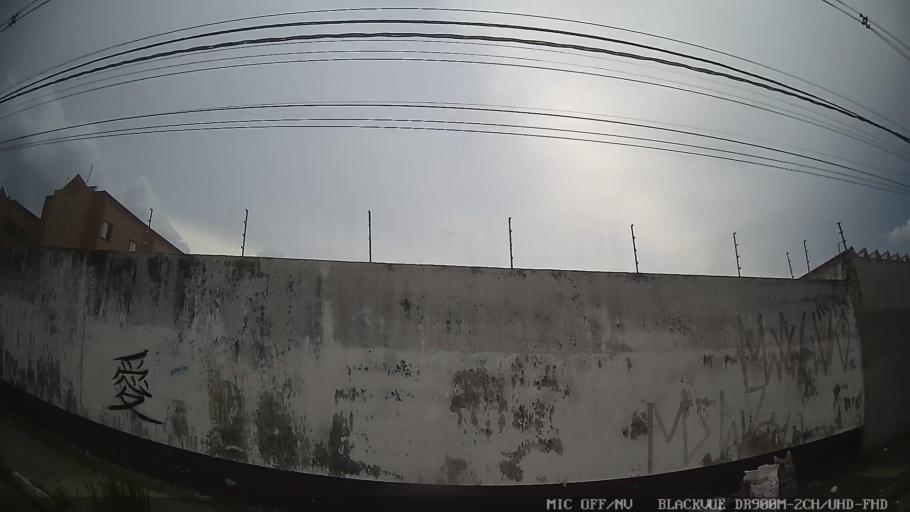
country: BR
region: Sao Paulo
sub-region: Suzano
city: Suzano
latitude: -23.5441
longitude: -46.2989
